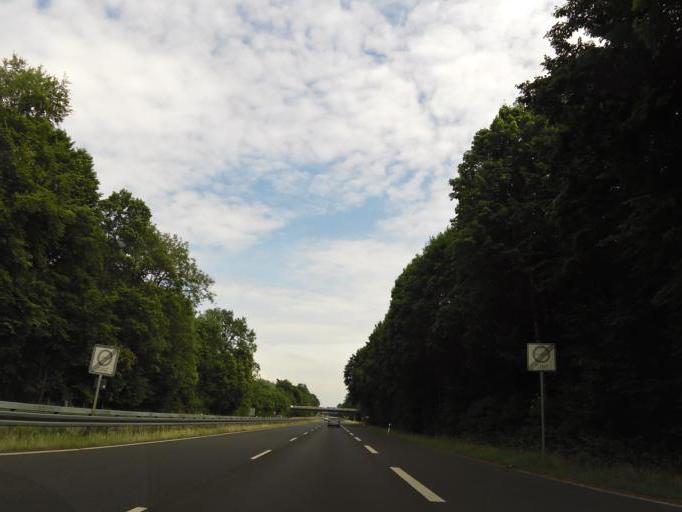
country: DE
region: Hesse
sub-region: Regierungsbezirk Darmstadt
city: Neu Isenburg
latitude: 50.0767
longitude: 8.7147
